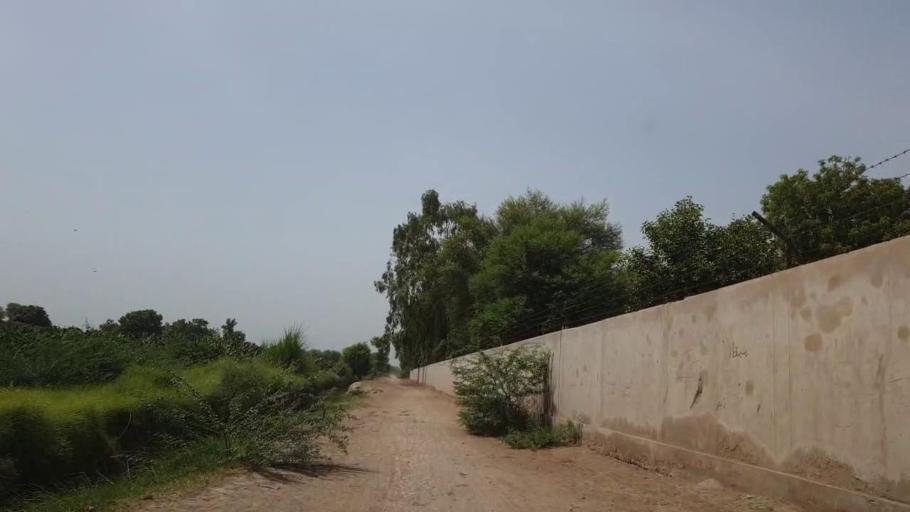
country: PK
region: Sindh
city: Sakrand
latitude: 26.1259
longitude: 68.2865
